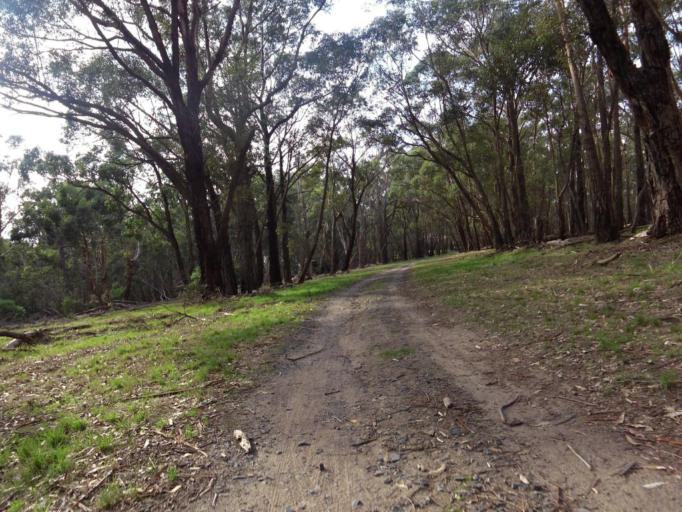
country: AU
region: Victoria
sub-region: Yarra Ranges
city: Lysterfield
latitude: -37.9445
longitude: 145.3041
